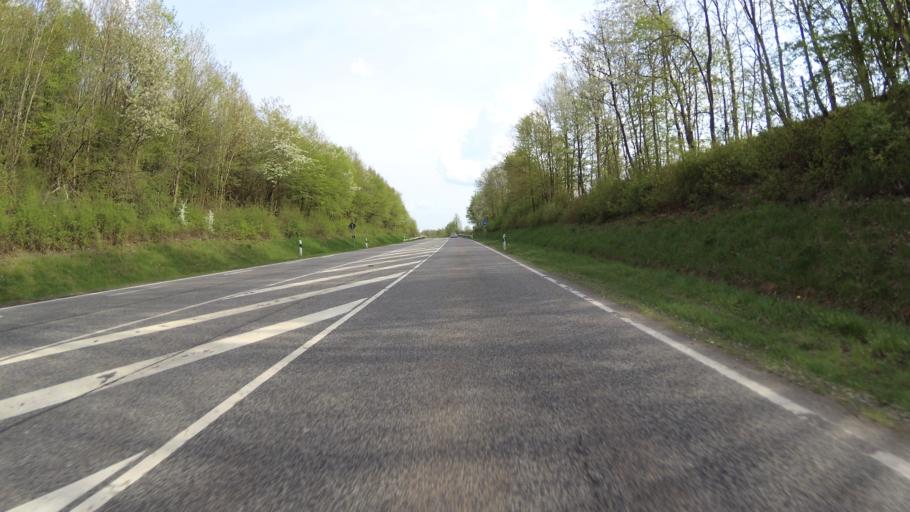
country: DE
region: Rheinland-Pfalz
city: Ulmen
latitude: 50.2099
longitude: 6.9727
